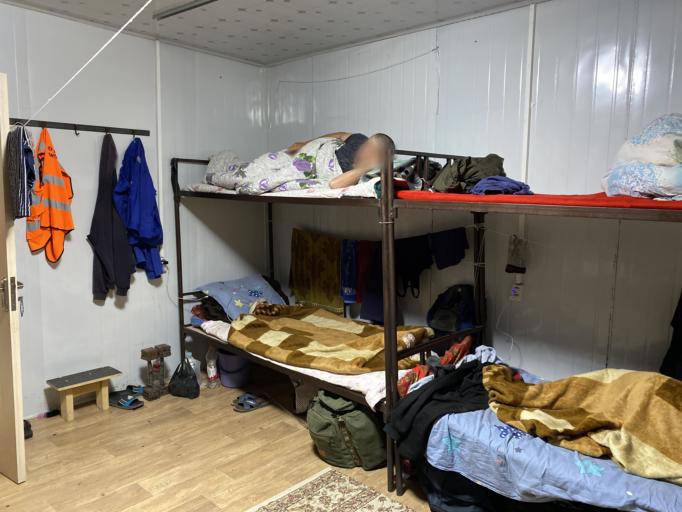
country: KZ
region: Qaraghandy
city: Balqash
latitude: 46.6449
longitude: 74.3946
